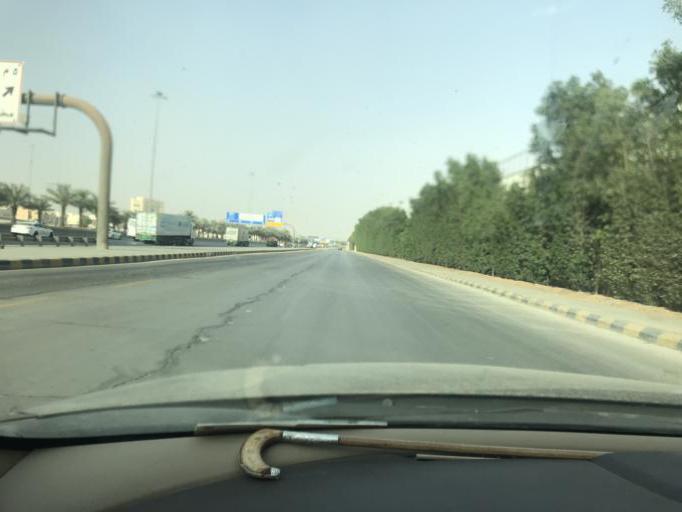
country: SA
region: Ar Riyad
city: Riyadh
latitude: 24.7868
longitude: 46.7097
